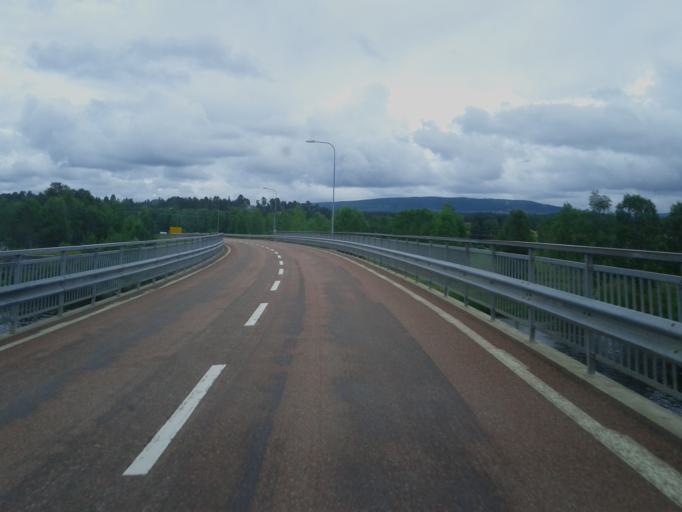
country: NO
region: Hedmark
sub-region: Trysil
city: Innbygda
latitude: 61.8528
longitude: 12.7123
